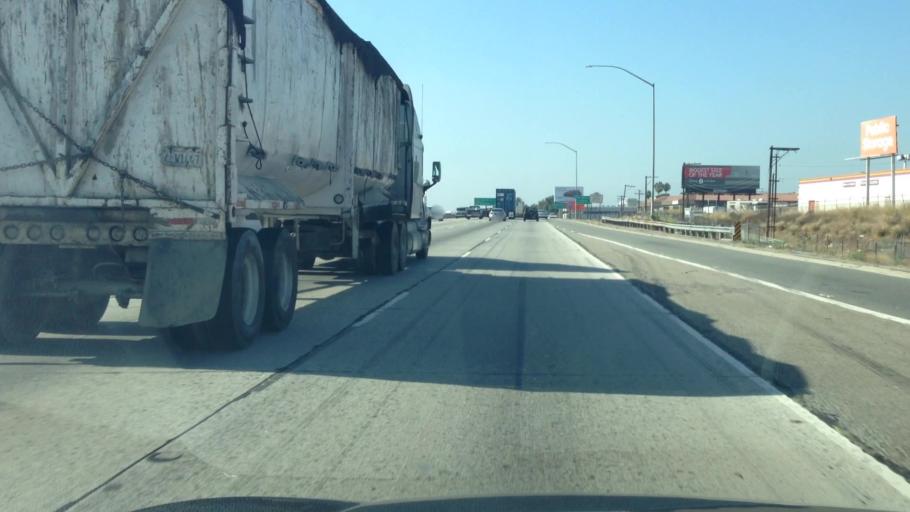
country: US
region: California
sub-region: Los Angeles County
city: West Carson
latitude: 33.8065
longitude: -118.2884
